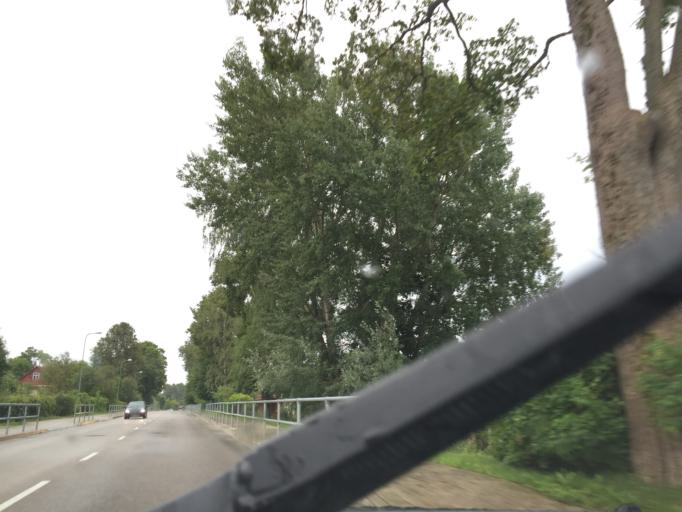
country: LV
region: Jekabpils Rajons
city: Jekabpils
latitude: 56.5015
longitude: 25.8881
